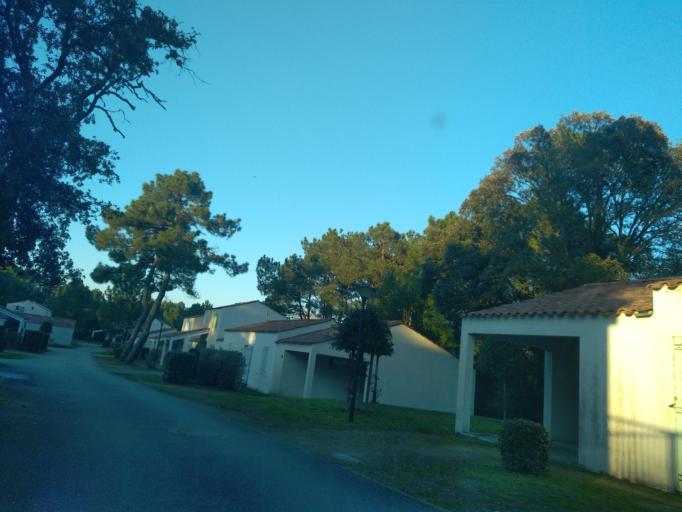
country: FR
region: Pays de la Loire
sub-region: Departement de la Vendee
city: Longeville-sur-Mer
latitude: 46.3898
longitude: -1.4824
